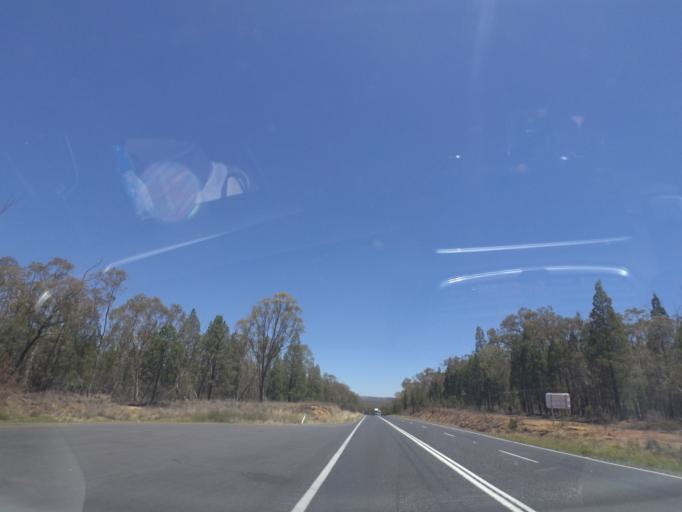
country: AU
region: New South Wales
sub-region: Warrumbungle Shire
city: Coonabarabran
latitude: -31.2346
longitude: 149.3170
